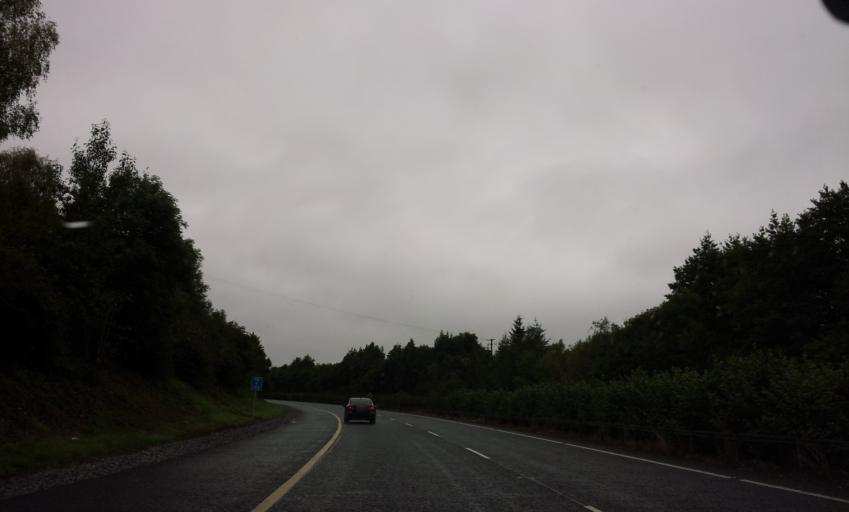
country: IE
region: Munster
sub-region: County Cork
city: Passage West
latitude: 51.9090
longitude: -8.3829
